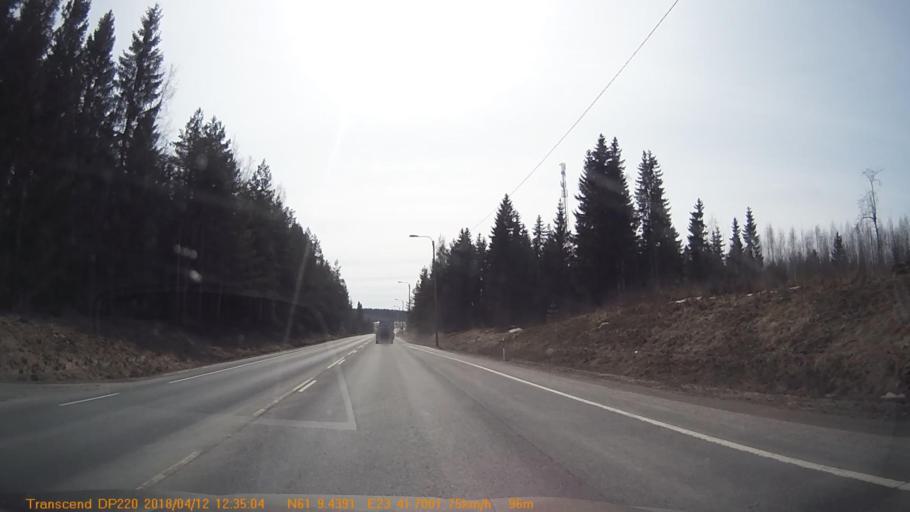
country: FI
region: Pirkanmaa
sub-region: Etelae-Pirkanmaa
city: Kylmaekoski
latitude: 61.1575
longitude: 23.6950
